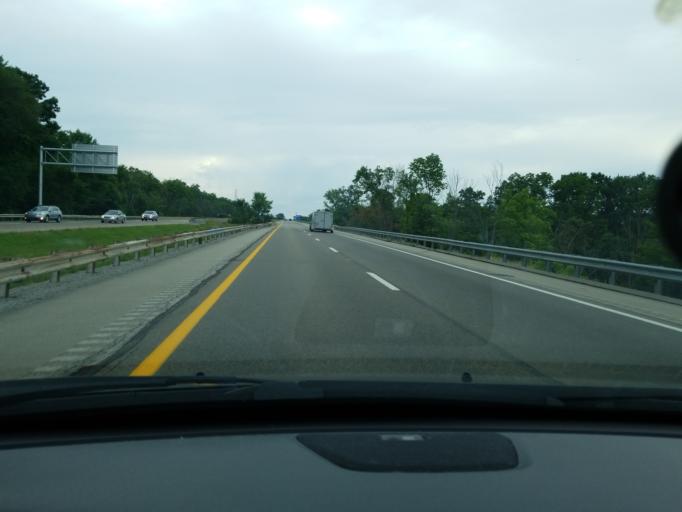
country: US
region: Ohio
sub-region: Mahoning County
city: New Middletown
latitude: 40.9323
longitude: -80.5705
